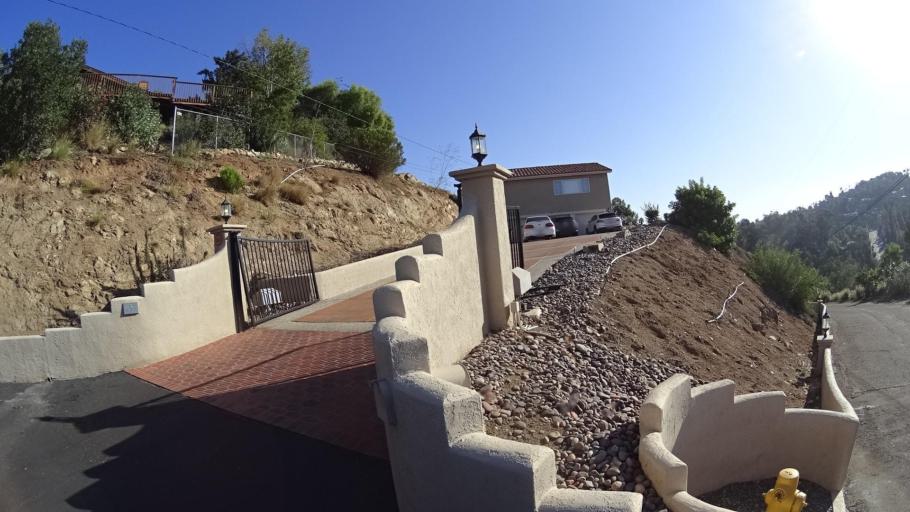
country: US
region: California
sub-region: San Diego County
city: Casa de Oro-Mount Helix
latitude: 32.7719
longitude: -116.9901
